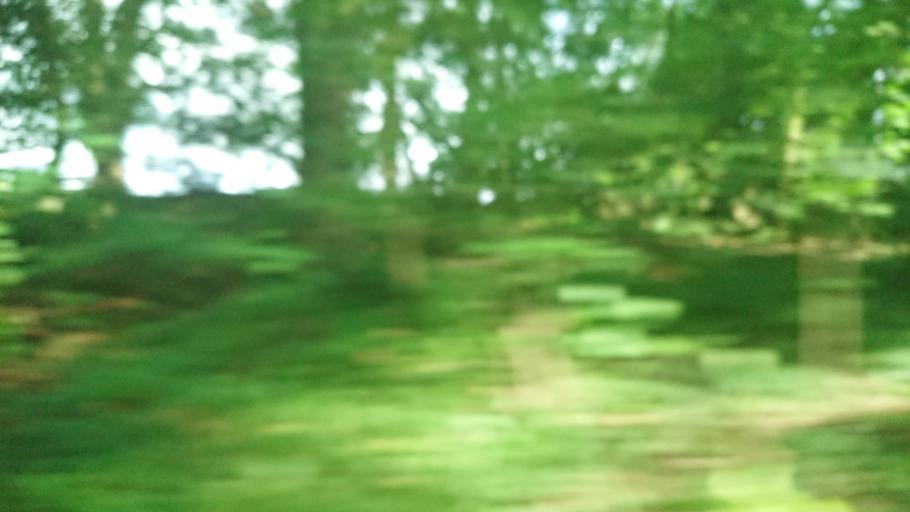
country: GB
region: England
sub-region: North Yorkshire
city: High Bentham
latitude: 54.1395
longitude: -2.5039
